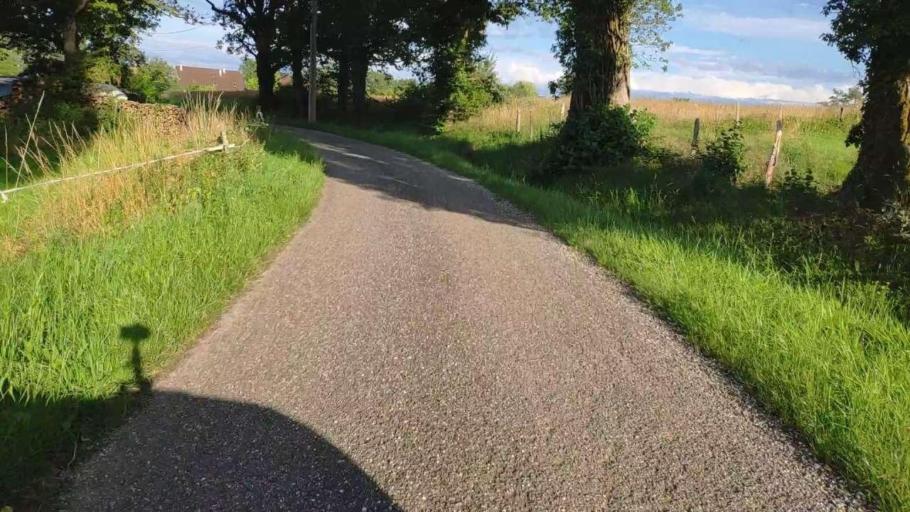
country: FR
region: Franche-Comte
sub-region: Departement du Jura
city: Bletterans
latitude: 46.7847
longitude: 5.5098
